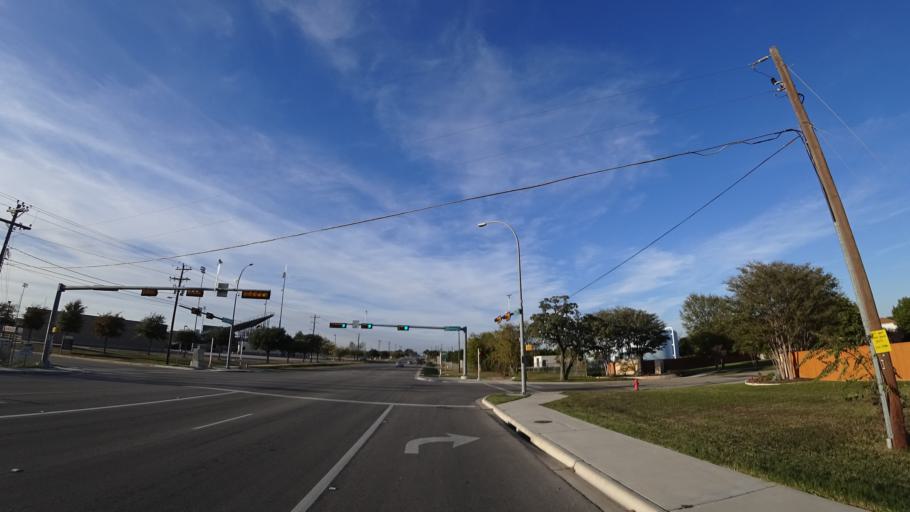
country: US
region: Texas
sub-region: Williamson County
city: Cedar Park
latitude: 30.5359
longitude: -97.8474
